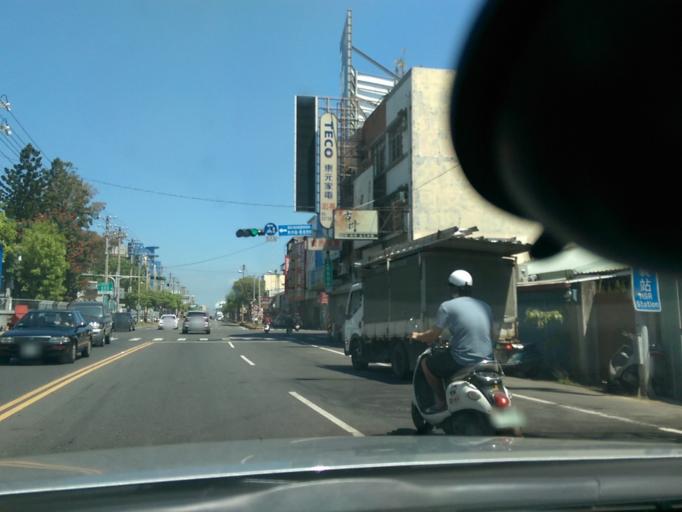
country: TW
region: Taiwan
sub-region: Chiayi
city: Jiayi Shi
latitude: 23.4656
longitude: 120.4547
